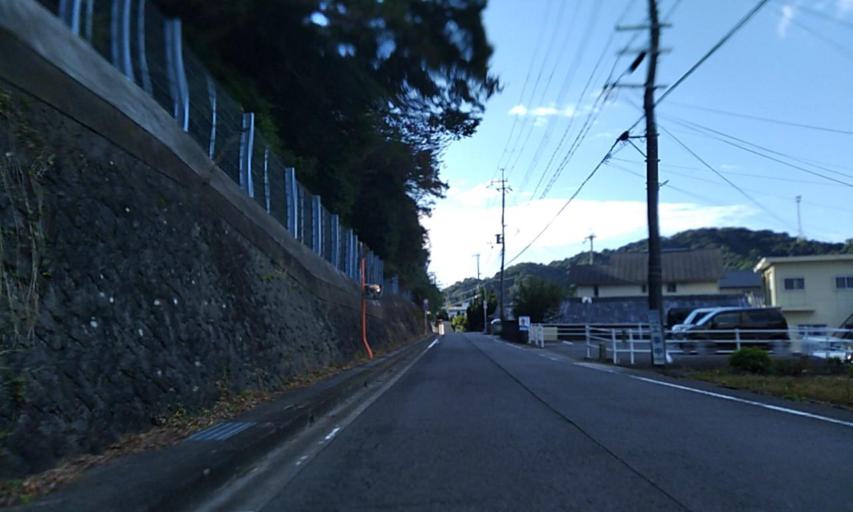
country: JP
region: Wakayama
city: Minato
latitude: 34.2781
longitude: 135.0758
